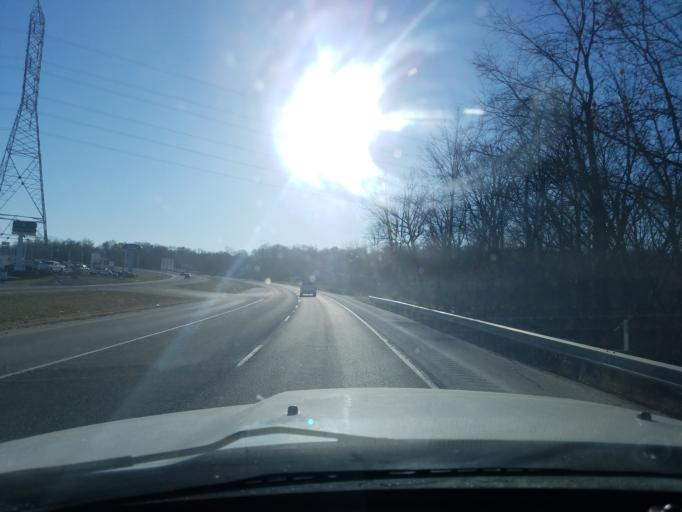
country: US
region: Indiana
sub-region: Lawrence County
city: Bedford
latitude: 38.8235
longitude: -86.5174
